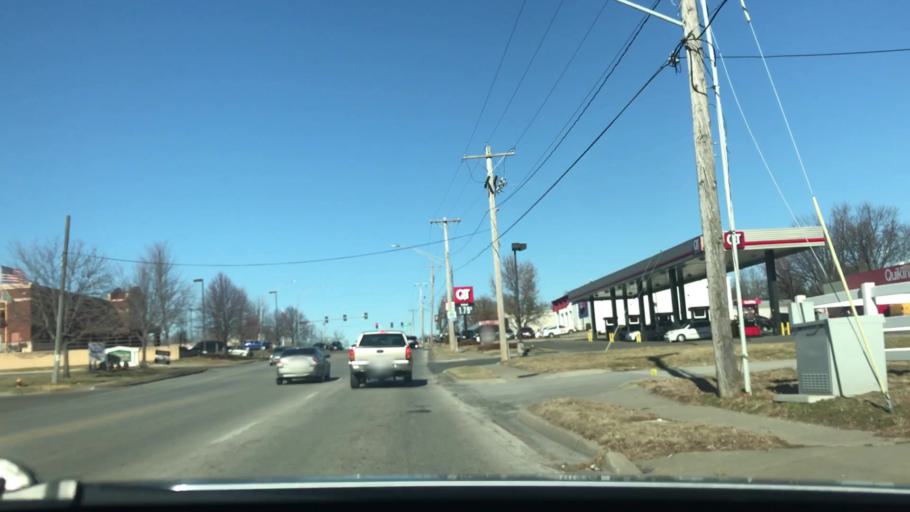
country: US
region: Missouri
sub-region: Jackson County
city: Independence
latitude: 39.0767
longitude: -94.3907
